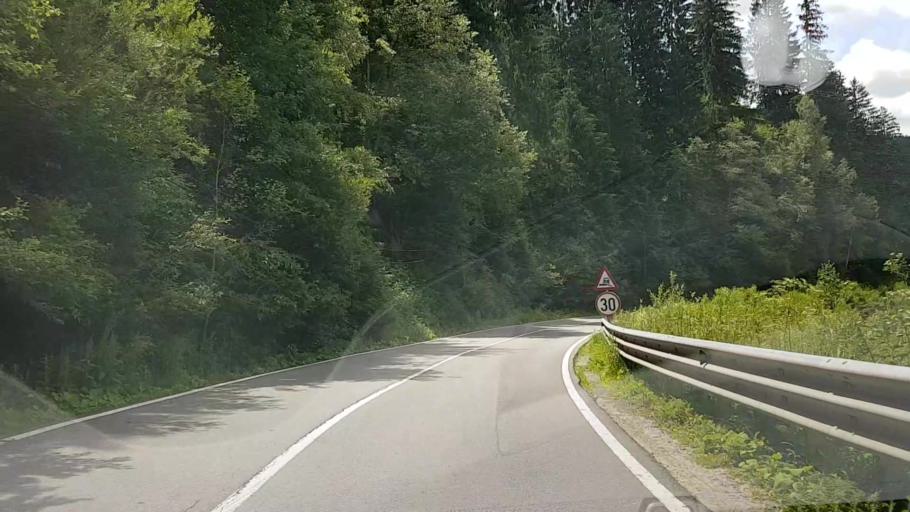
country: RO
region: Suceava
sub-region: Comuna Crucea
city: Crucea
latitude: 47.3524
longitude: 25.6153
